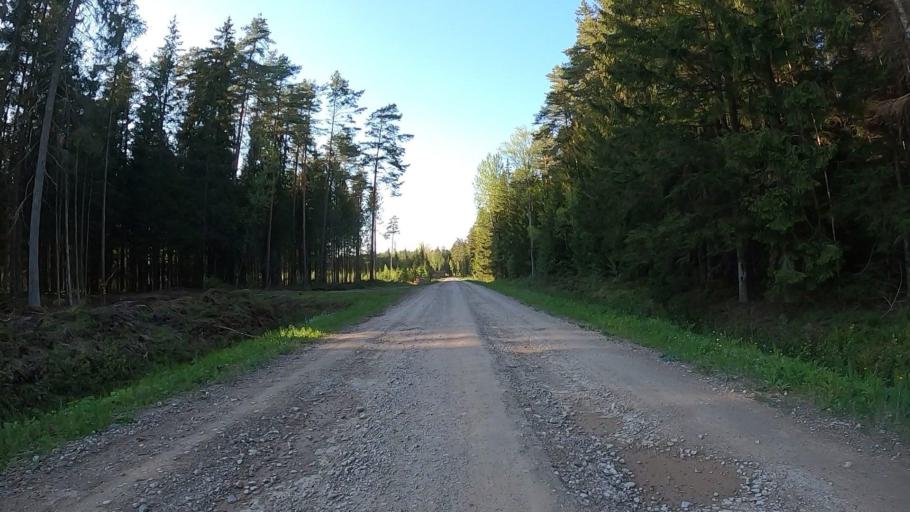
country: LV
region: Kekava
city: Kekava
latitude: 56.7538
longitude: 24.2310
